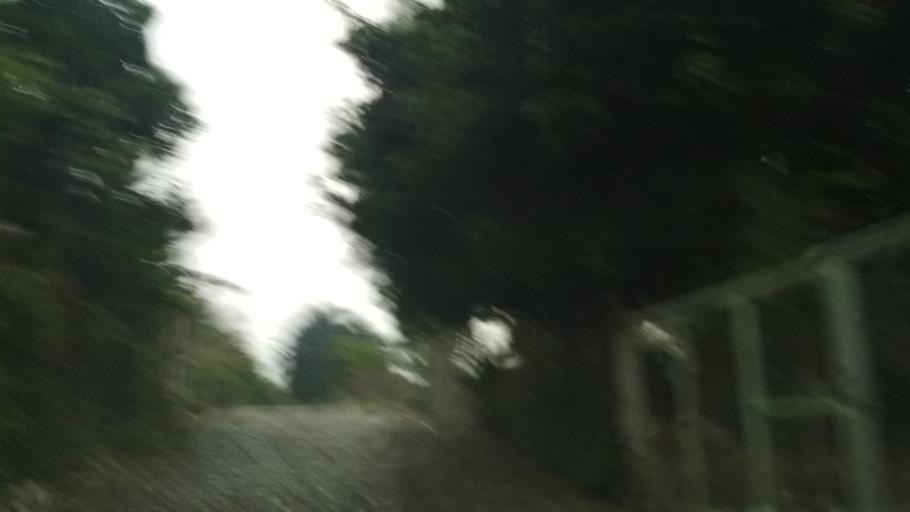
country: MM
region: Shan
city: Taunggyi
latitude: 20.3049
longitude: 97.3056
